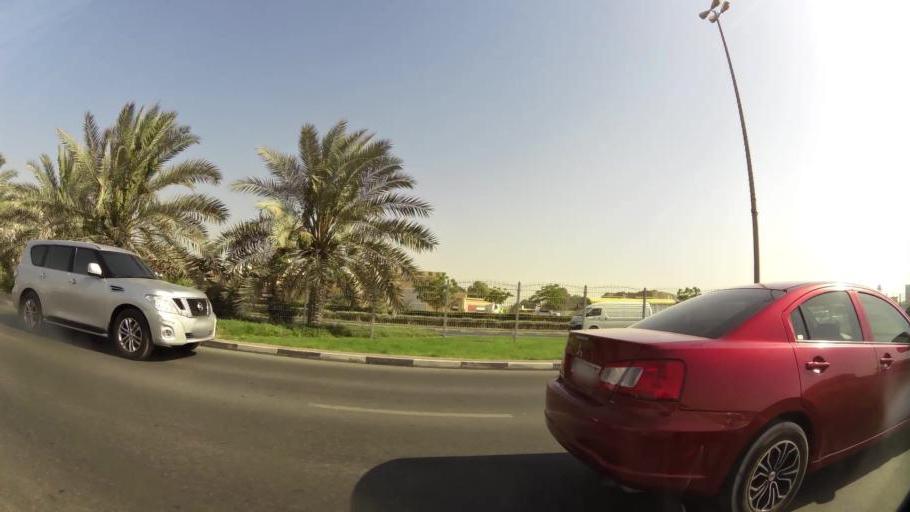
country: AE
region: Ajman
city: Ajman
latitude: 25.3952
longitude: 55.4886
